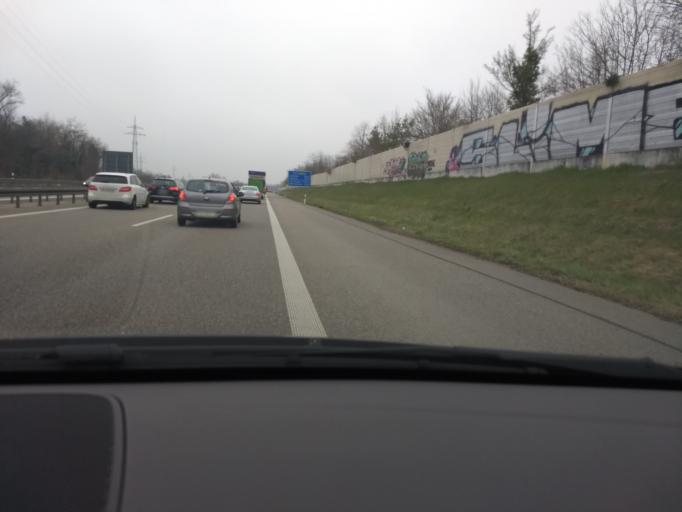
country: FR
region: Alsace
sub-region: Departement du Haut-Rhin
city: Kembs
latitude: 47.6847
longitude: 7.5222
